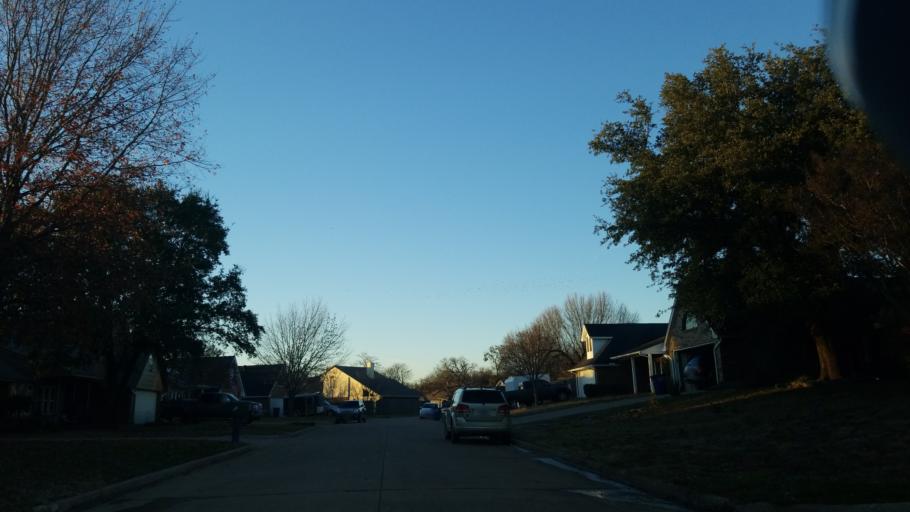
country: US
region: Texas
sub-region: Denton County
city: Hickory Creek
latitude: 33.1386
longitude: -97.0532
